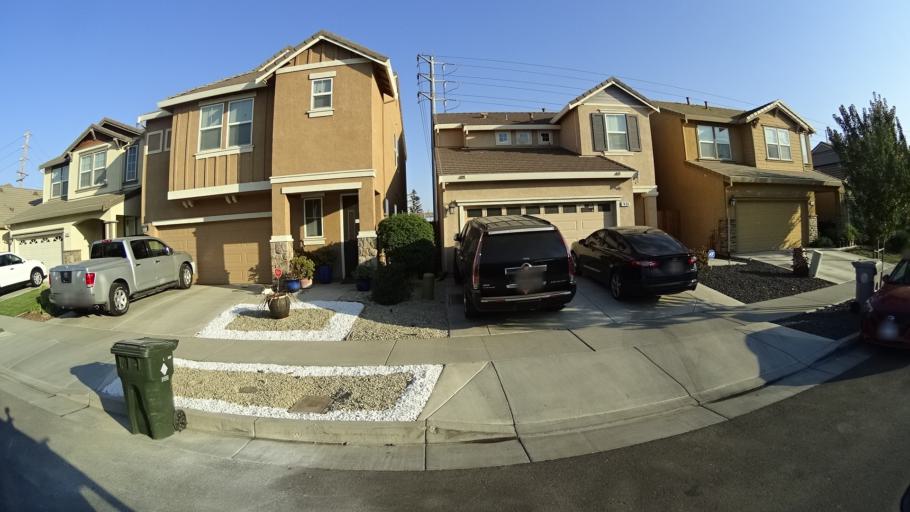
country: US
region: California
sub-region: Sacramento County
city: Parkway
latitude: 38.4885
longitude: -121.4697
